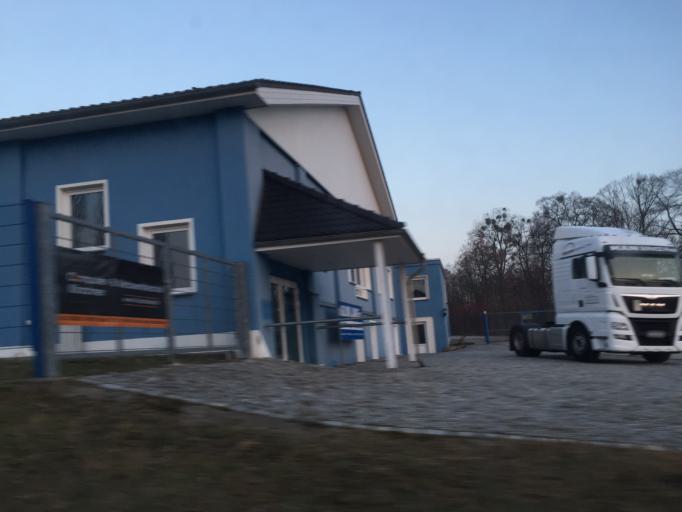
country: DE
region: Saxony
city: Pirna
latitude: 50.9758
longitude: 13.9422
